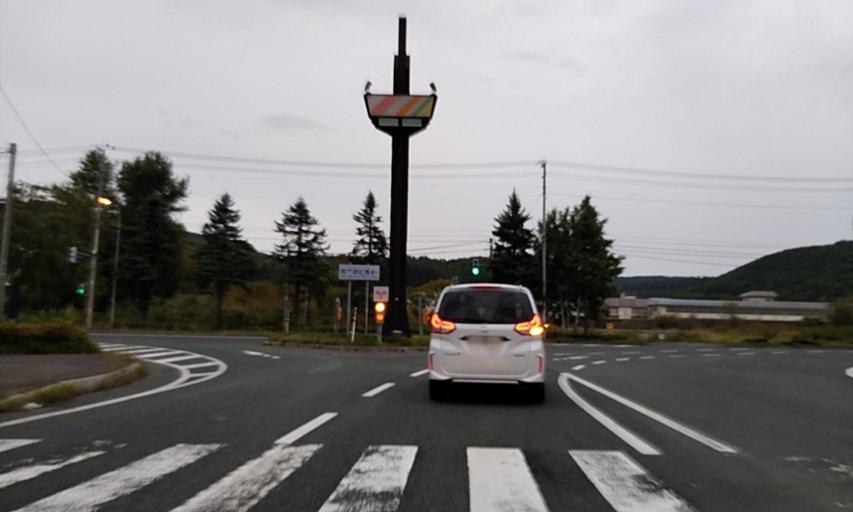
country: JP
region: Hokkaido
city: Abashiri
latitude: 44.0127
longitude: 144.2313
